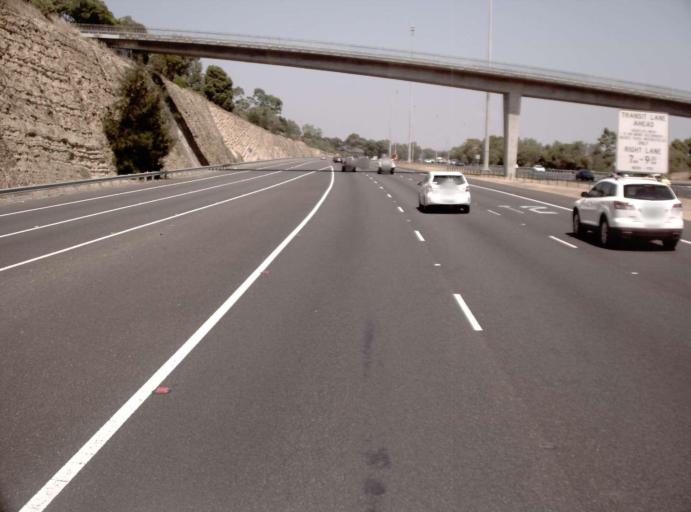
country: AU
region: Victoria
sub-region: Manningham
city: Bulleen
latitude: -37.7814
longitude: 145.0761
